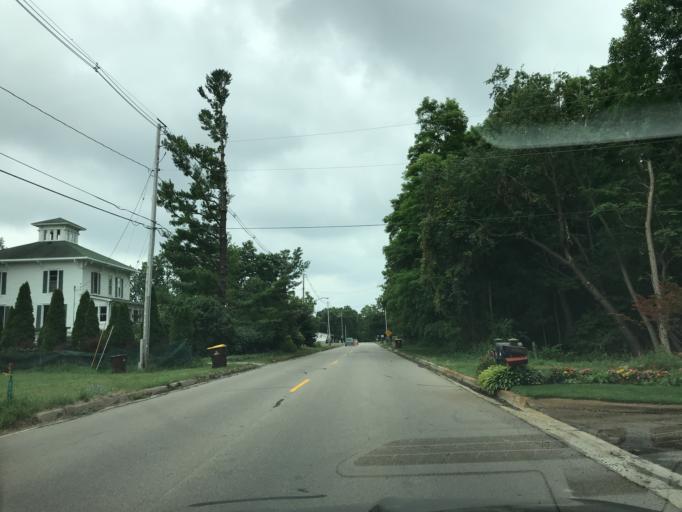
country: US
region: Michigan
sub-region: Eaton County
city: Waverly
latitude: 42.7673
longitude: -84.6475
